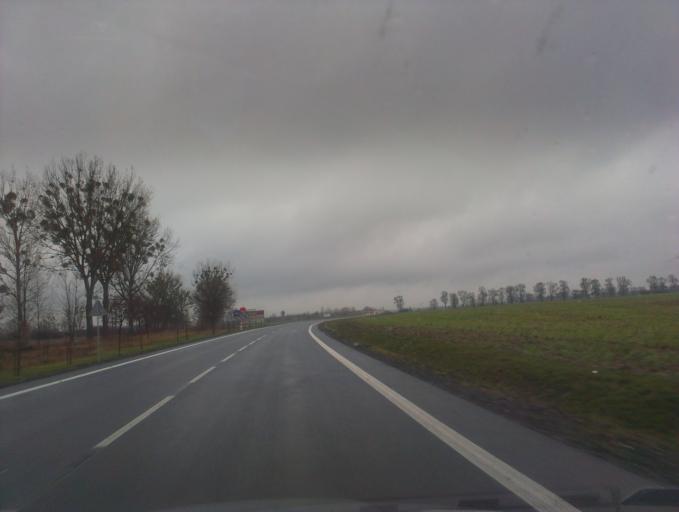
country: PL
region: Greater Poland Voivodeship
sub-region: Powiat obornicki
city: Oborniki
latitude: 52.5957
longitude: 16.8239
